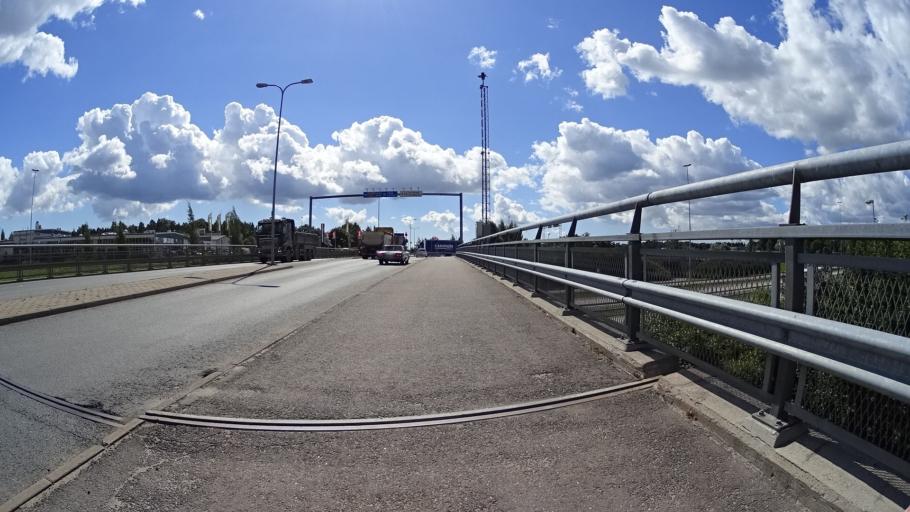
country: FI
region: Uusimaa
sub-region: Helsinki
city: Teekkarikylae
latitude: 60.2983
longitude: 24.8841
